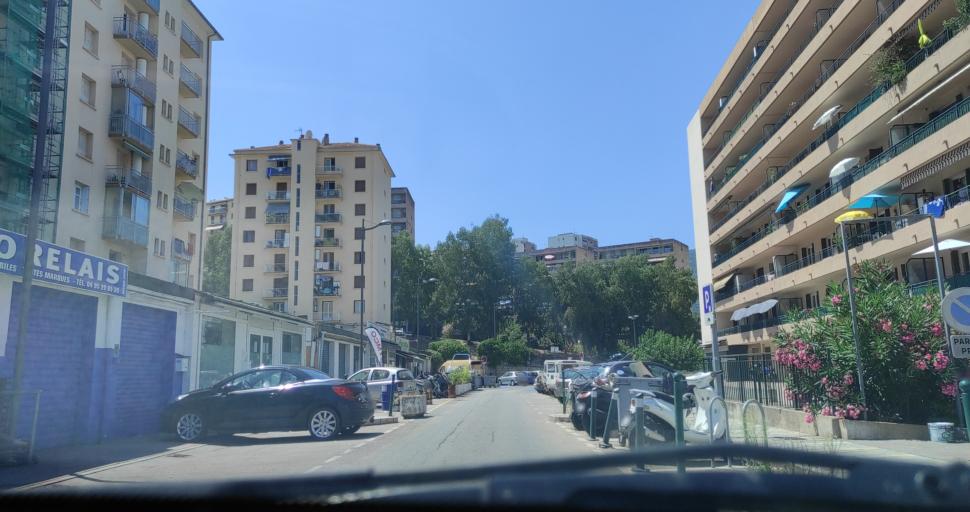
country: FR
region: Corsica
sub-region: Departement de la Corse-du-Sud
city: Ajaccio
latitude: 41.9343
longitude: 8.7380
